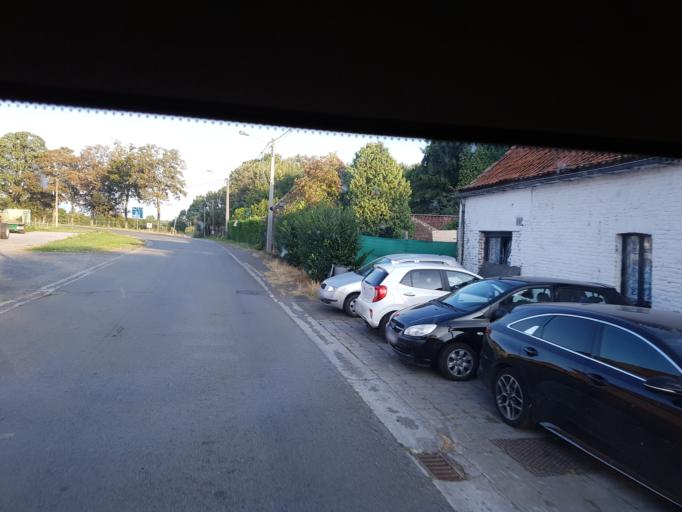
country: FR
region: Nord-Pas-de-Calais
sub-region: Departement du Nord
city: Flines-les-Mortagne
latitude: 50.5410
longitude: 3.5055
